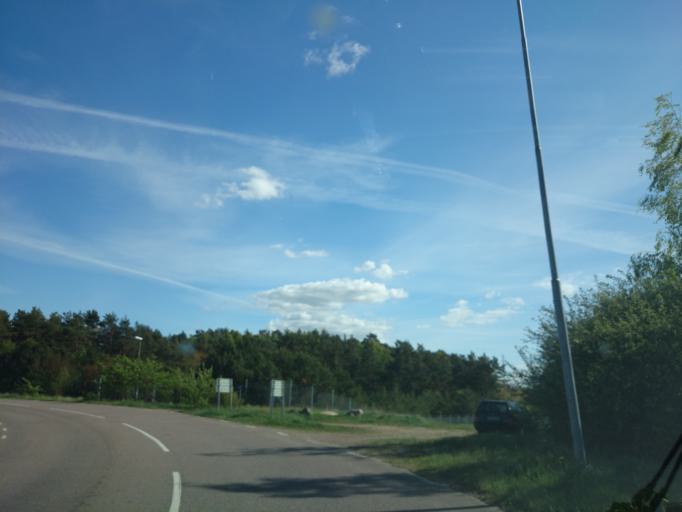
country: SE
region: Skane
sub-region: Kavlinge Kommun
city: Kaevlinge
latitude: 55.7841
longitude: 13.1117
